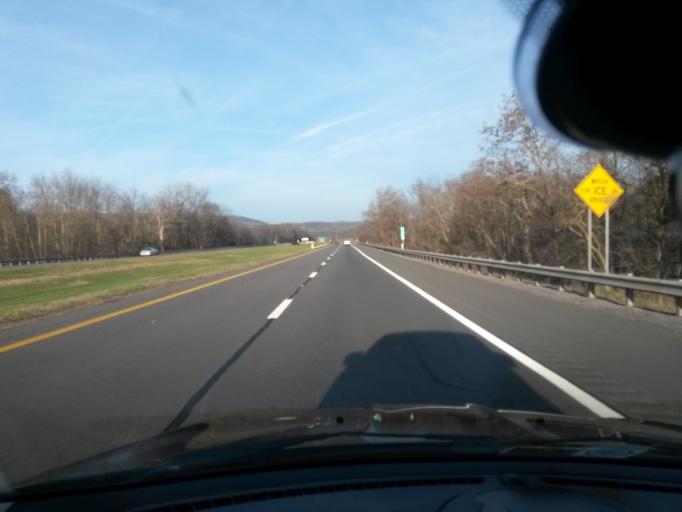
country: US
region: West Virginia
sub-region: Greenbrier County
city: Lewisburg
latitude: 37.8448
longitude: -80.4765
